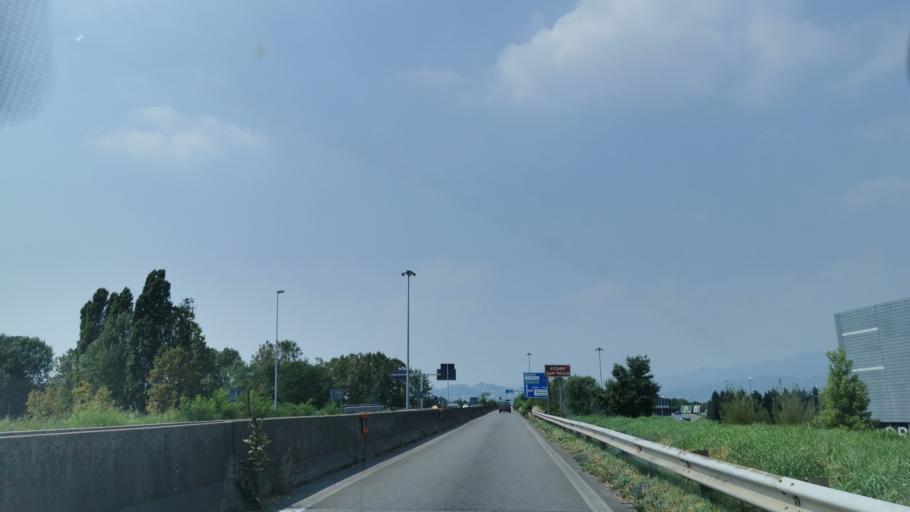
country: IT
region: Lombardy
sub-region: Provincia di Bergamo
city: Orio al Serio
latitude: 45.6626
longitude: 9.6926
